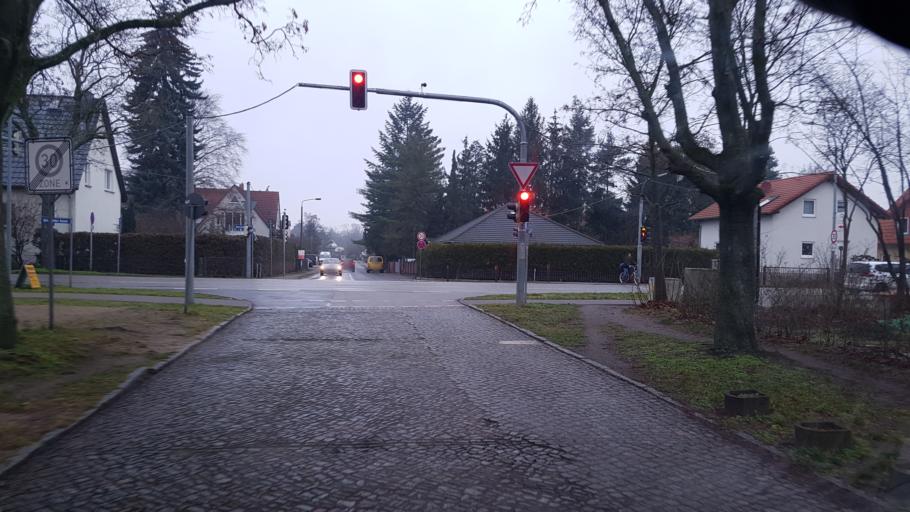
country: DE
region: Brandenburg
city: Stahnsdorf
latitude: 52.3782
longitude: 13.2084
